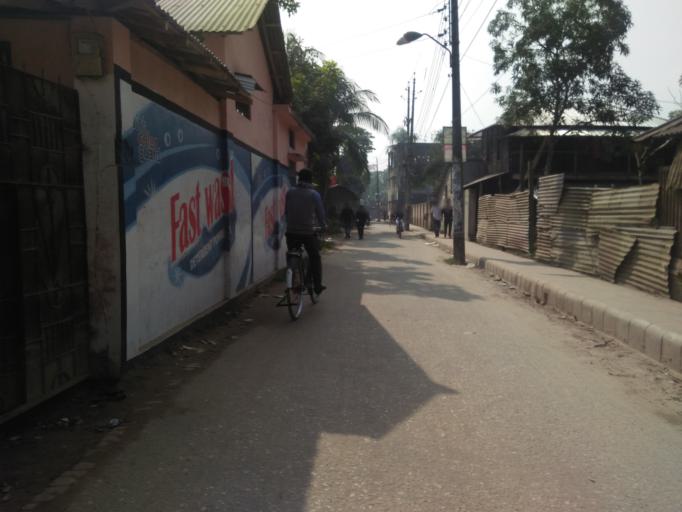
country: BD
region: Barisal
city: Bhola
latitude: 22.6841
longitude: 90.6427
